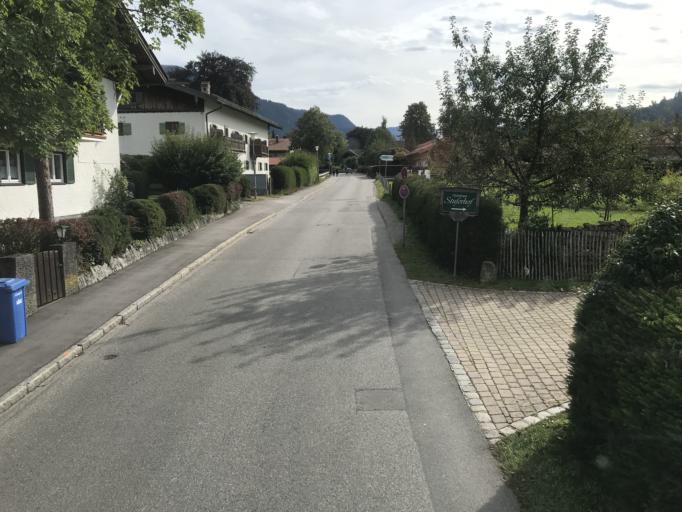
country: DE
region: Bavaria
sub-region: Upper Bavaria
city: Rottach-Egern
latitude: 47.6948
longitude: 11.7599
